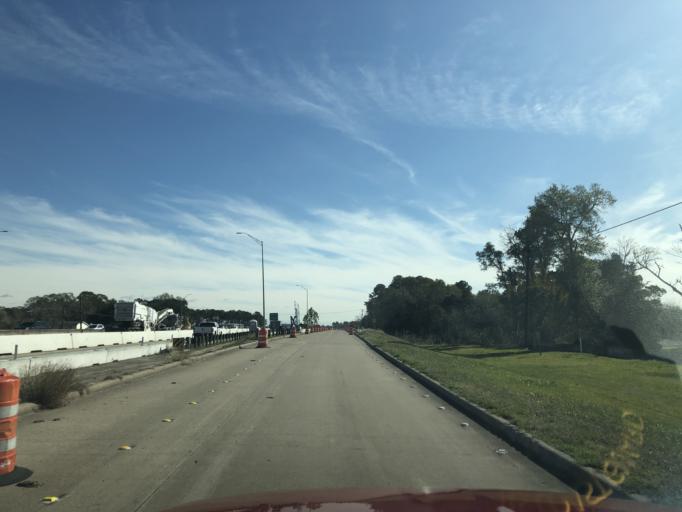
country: US
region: Texas
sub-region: Galveston County
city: Dickinson
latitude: 29.4462
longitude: -95.0750
